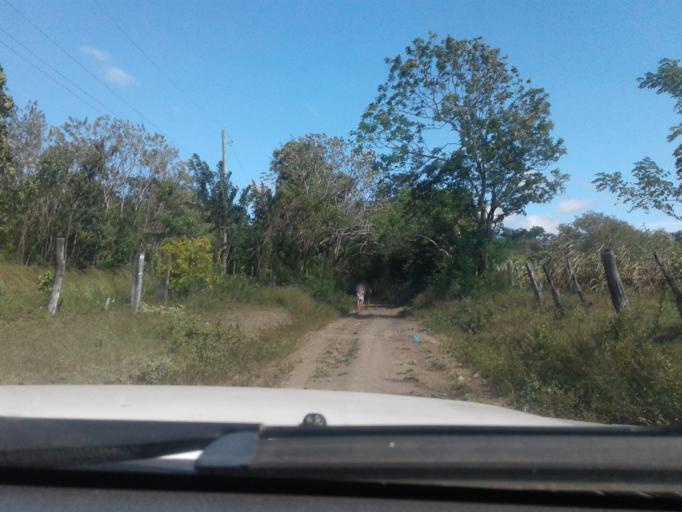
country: NI
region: Carazo
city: Santa Teresa
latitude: 11.7643
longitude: -86.1790
